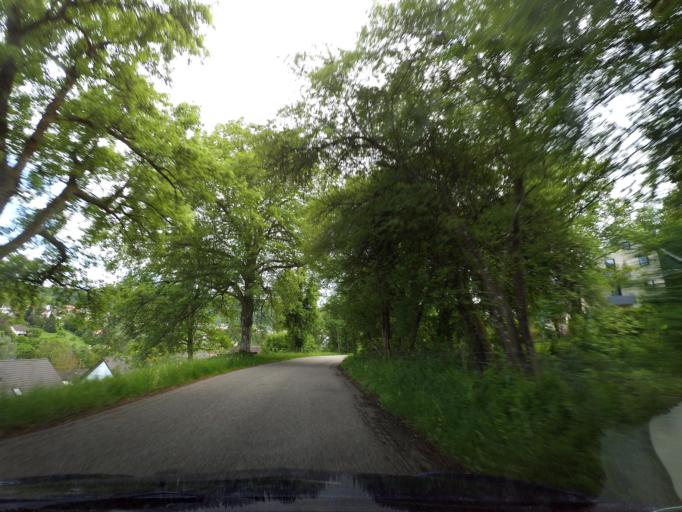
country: DE
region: Baden-Wuerttemberg
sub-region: Regierungsbezirk Stuttgart
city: Murrhardt
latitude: 48.9879
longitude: 9.5823
